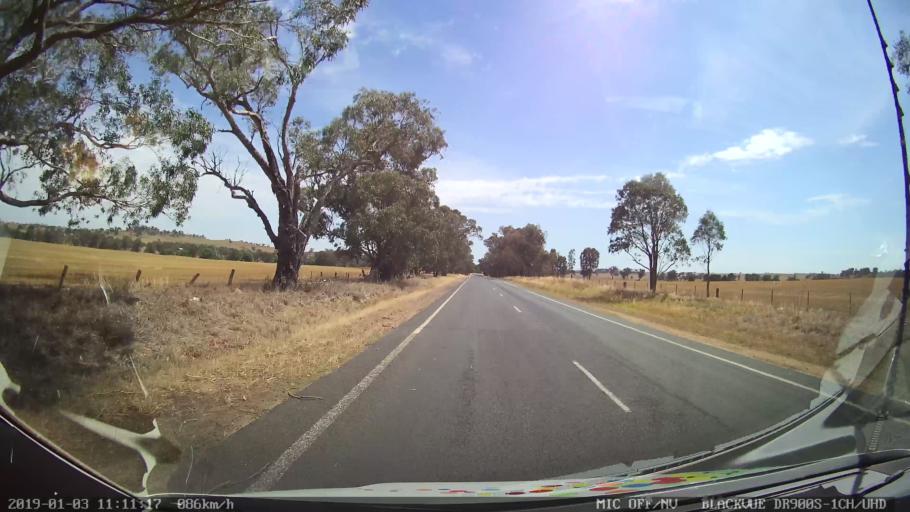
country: AU
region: New South Wales
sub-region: Young
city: Young
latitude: -34.2165
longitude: 148.2596
